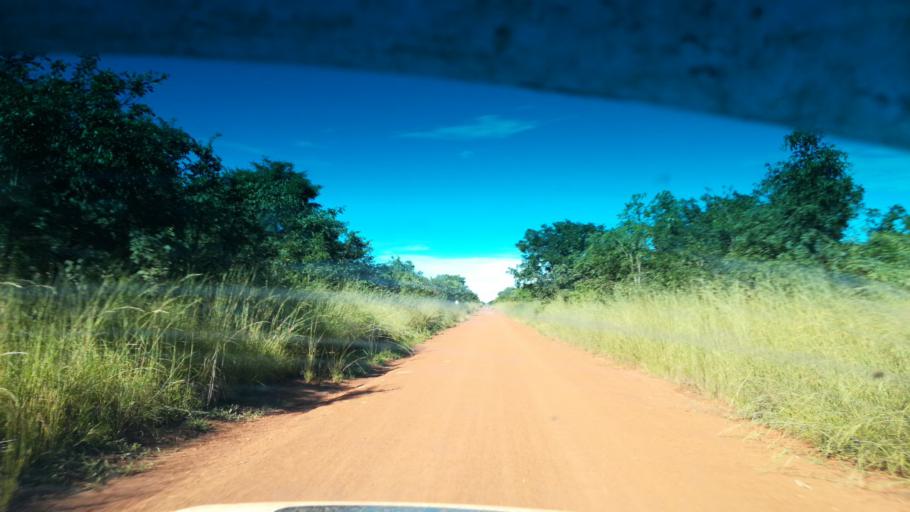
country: ZM
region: Luapula
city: Nchelenge
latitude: -9.3107
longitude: 28.2562
